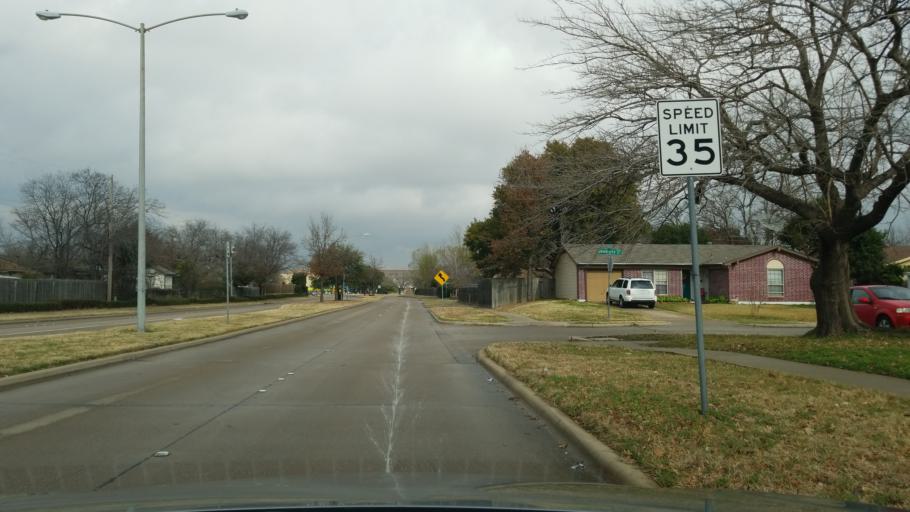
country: US
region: Texas
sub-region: Denton County
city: Lewisville
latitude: 33.0352
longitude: -97.0188
